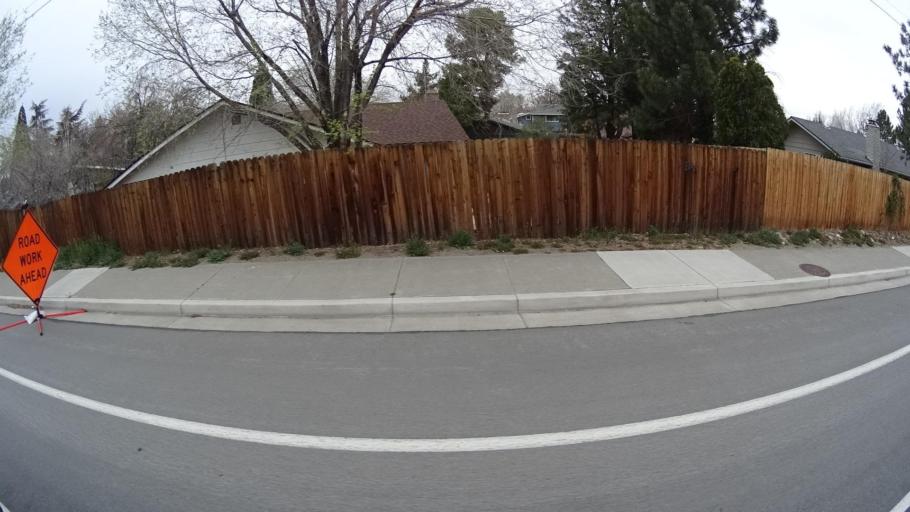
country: US
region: Nevada
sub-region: Washoe County
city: Reno
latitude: 39.5071
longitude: -119.8449
